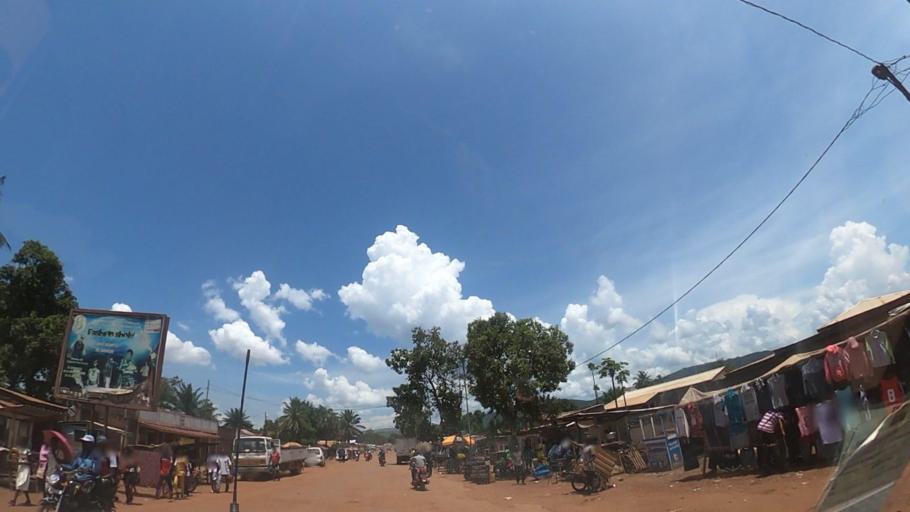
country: CF
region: Bangui
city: Bangui
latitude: 4.3609
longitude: 18.5608
